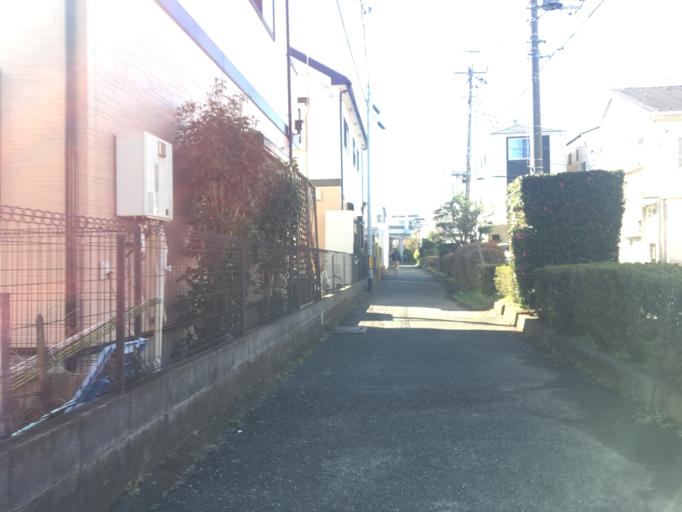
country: JP
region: Saitama
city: Shiki
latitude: 35.8058
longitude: 139.5668
